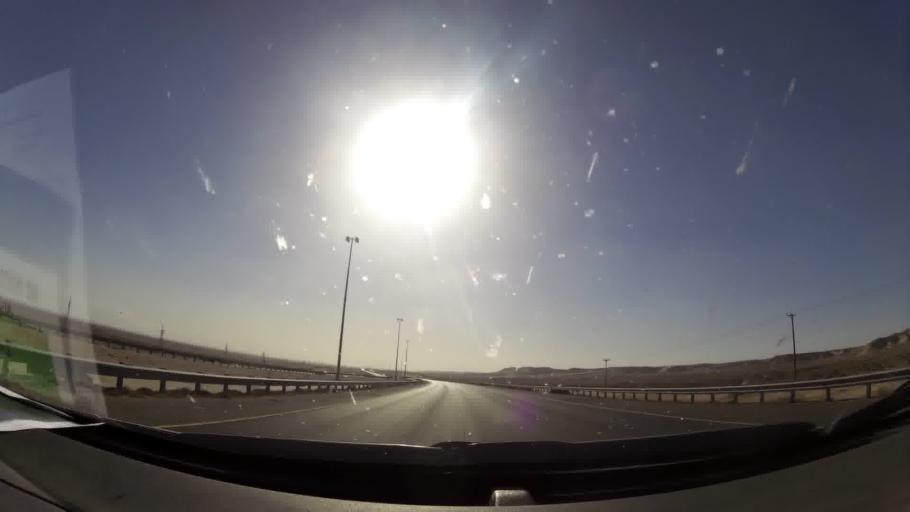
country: KW
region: Al Asimah
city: Kuwait City
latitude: 29.5168
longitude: 47.8068
